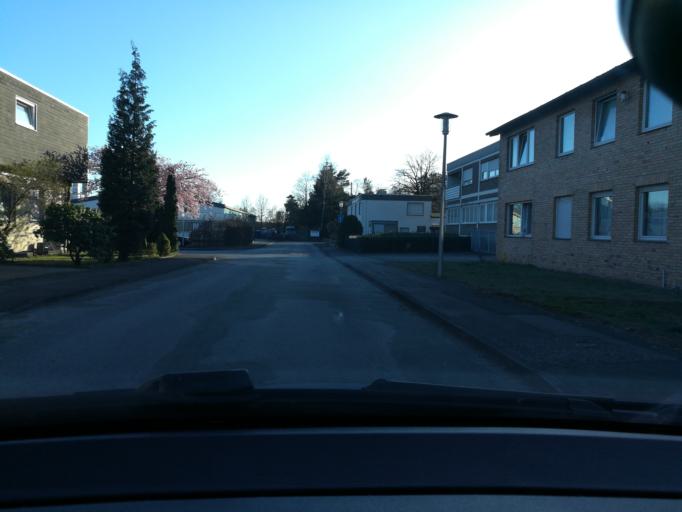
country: DE
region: North Rhine-Westphalia
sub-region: Regierungsbezirk Detmold
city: Oerlinghausen
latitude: 51.9560
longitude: 8.5754
